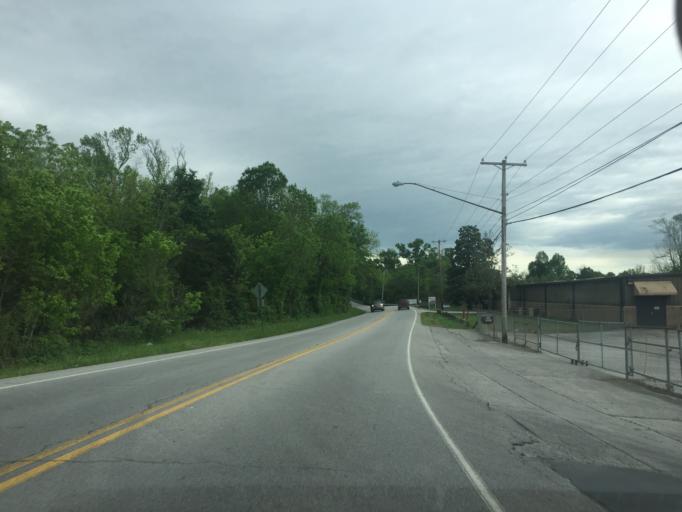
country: US
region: Tennessee
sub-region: Hamilton County
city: Harrison
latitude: 35.0657
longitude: -85.1570
